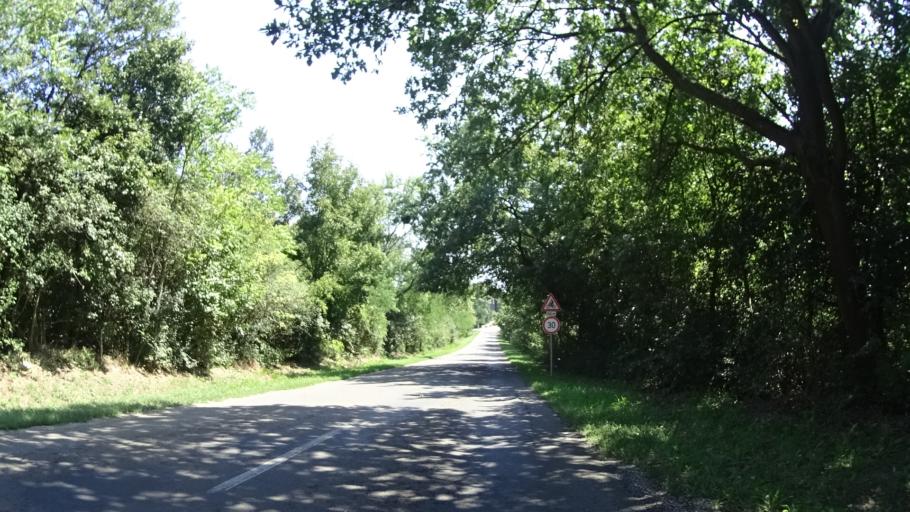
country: HU
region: Fejer
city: Pakozd
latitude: 47.2252
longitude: 18.5762
